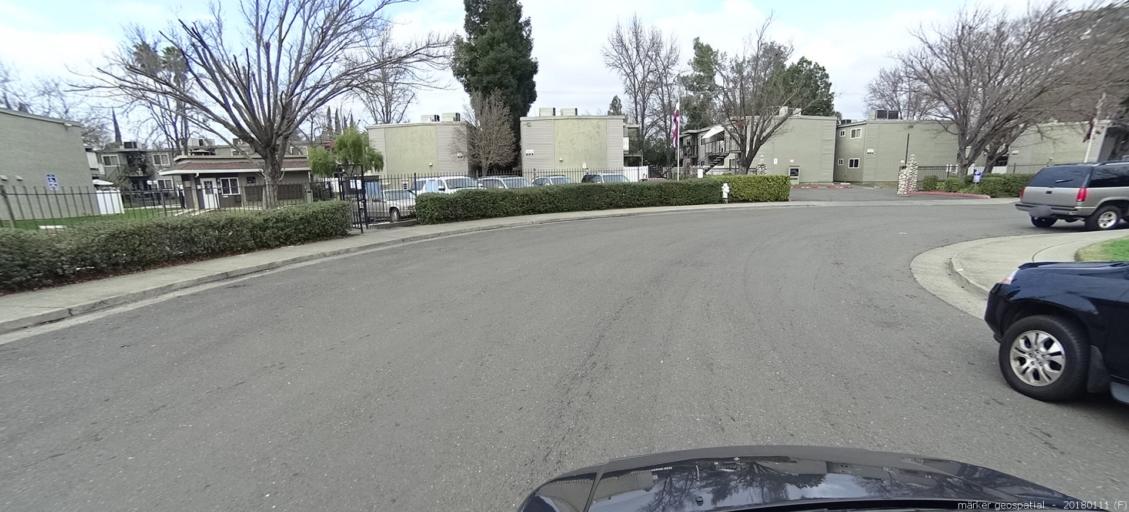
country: US
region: California
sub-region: Sacramento County
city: Rancho Cordova
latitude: 38.6145
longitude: -121.2889
